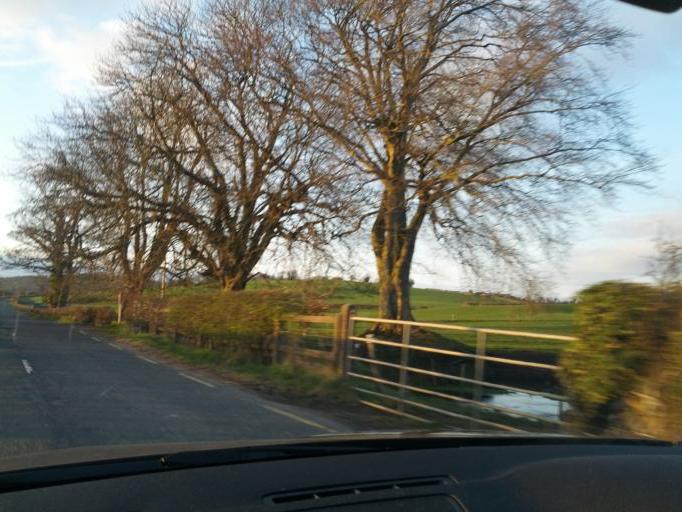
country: IE
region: Munster
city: Nenagh Bridge
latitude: 52.9573
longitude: -8.2352
